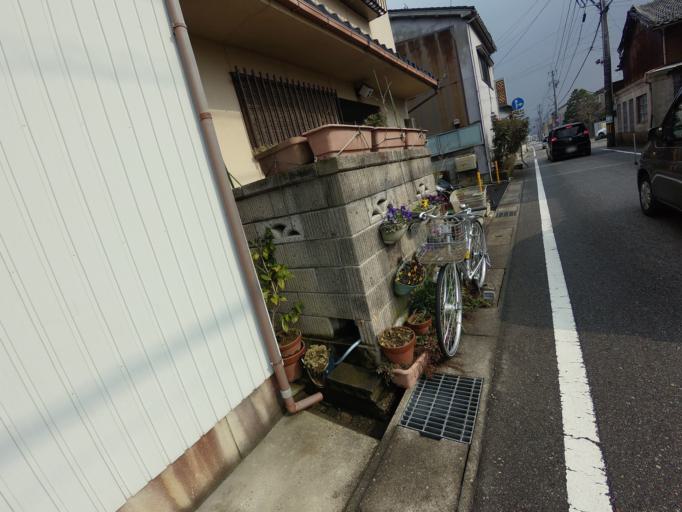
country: JP
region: Ishikawa
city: Nanao
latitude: 37.0482
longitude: 136.9632
